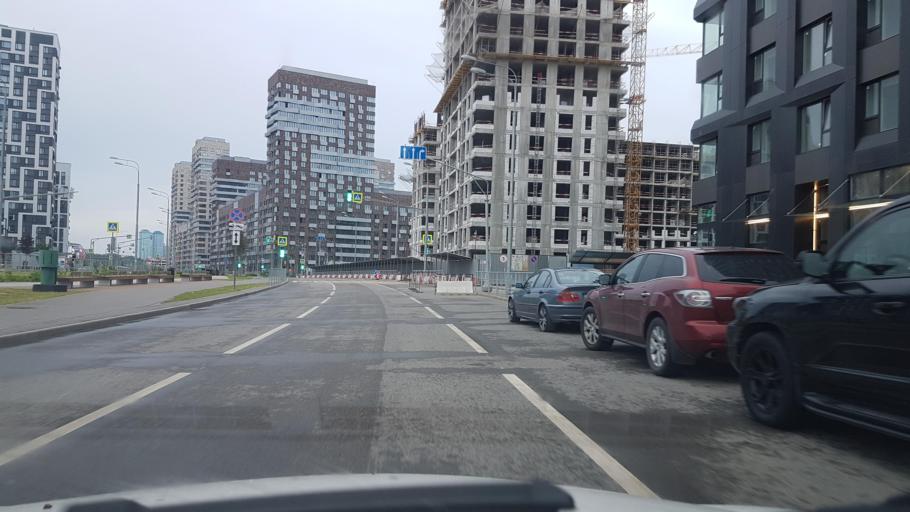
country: RU
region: Moscow
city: Strogino
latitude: 55.8205
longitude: 37.4246
